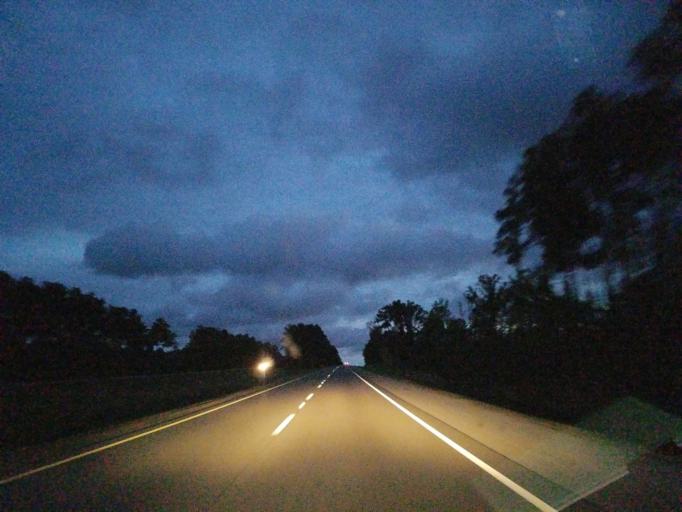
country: US
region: Mississippi
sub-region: Jones County
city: Sharon
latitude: 31.8651
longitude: -89.0468
